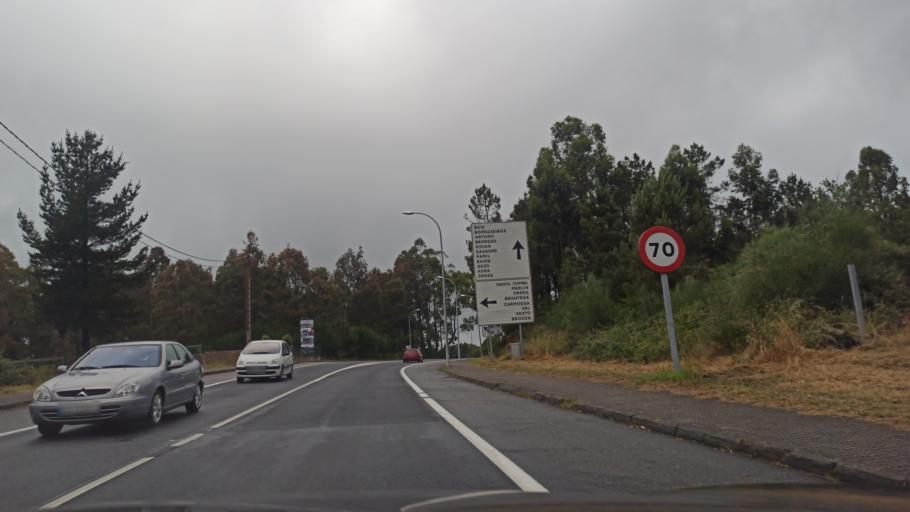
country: ES
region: Galicia
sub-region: Provincia da Coruna
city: Santiso
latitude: 42.7676
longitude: -8.0228
